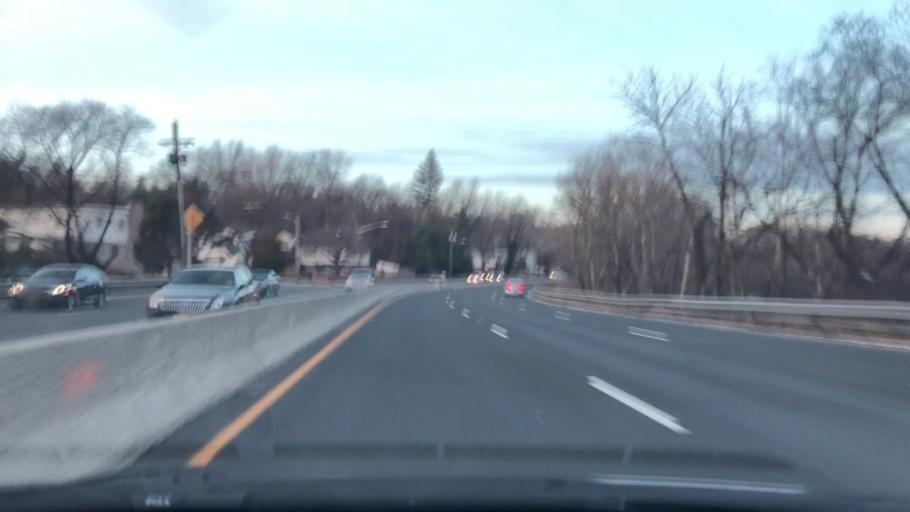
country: US
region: New Jersey
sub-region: Bergen County
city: Elmwood Park
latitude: 40.9116
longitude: -74.1341
